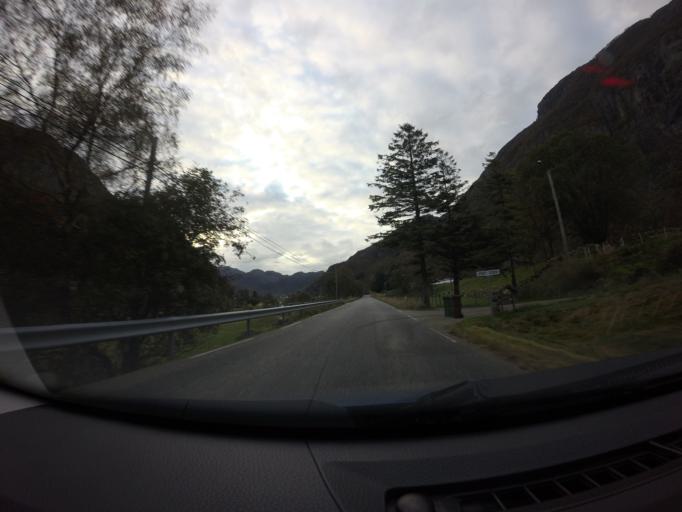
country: NO
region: Rogaland
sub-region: Forsand
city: Forsand
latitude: 58.8115
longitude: 6.2316
